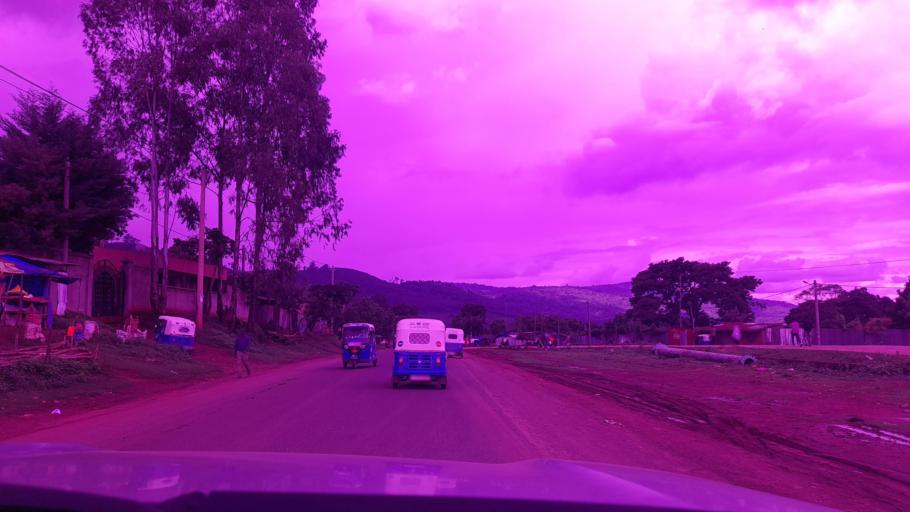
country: ET
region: Oromiya
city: Jima
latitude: 7.6699
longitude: 36.8583
